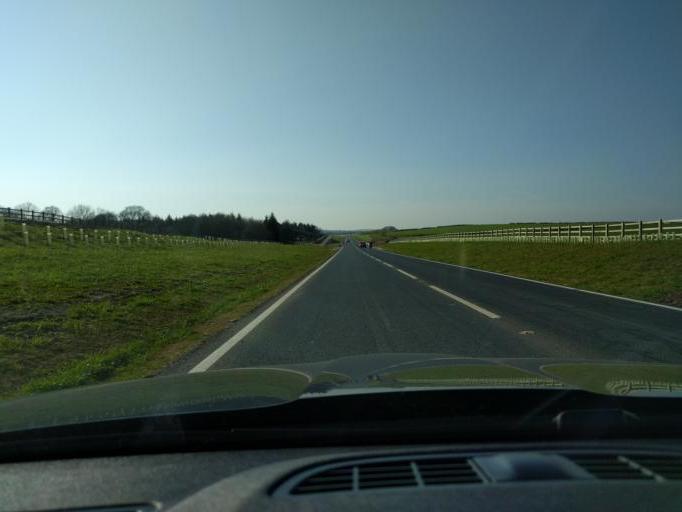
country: GB
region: England
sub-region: Northumberland
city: Hebron
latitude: 55.1806
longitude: -1.6731
